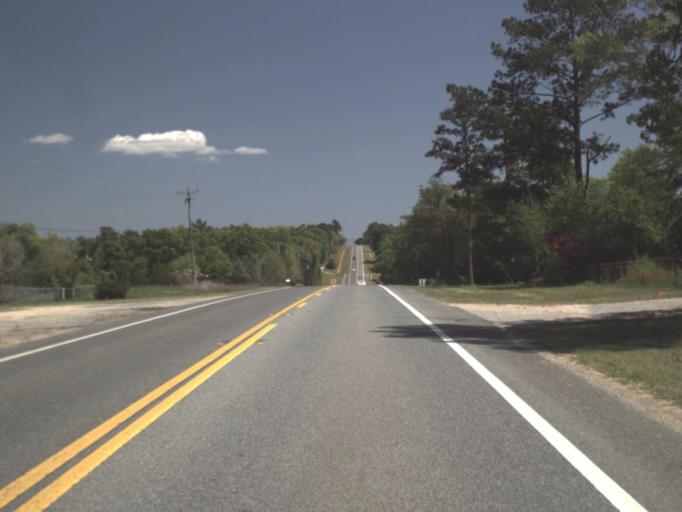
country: US
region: Florida
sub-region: Escambia County
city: Century
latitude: 30.9489
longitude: -87.1906
